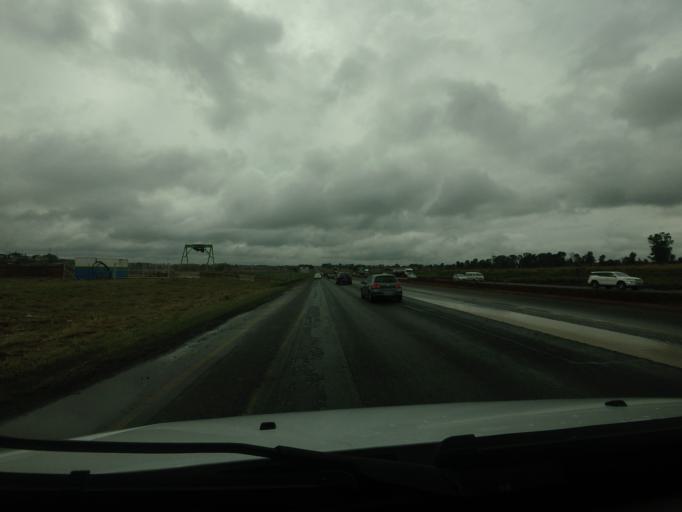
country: ZA
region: Mpumalanga
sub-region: Nkangala District Municipality
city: Witbank
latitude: -25.8805
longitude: 29.1702
